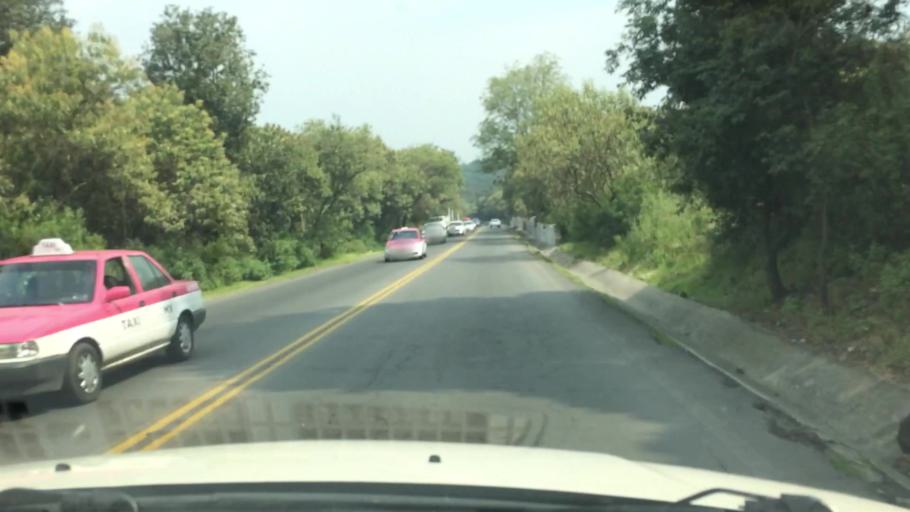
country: MX
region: Mexico City
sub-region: Tlalpan
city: Lomas de Tepemecatl
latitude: 19.2672
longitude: -99.2308
